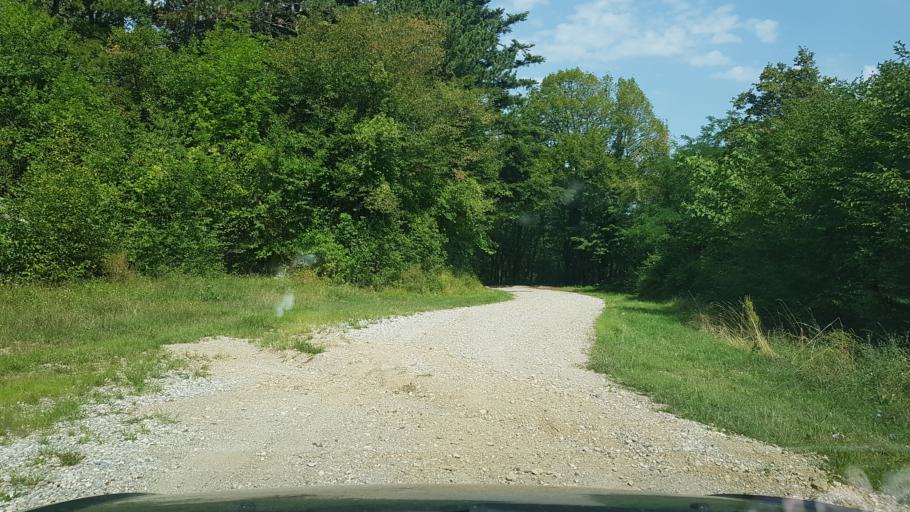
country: SI
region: Nova Gorica
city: Solkan
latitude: 46.0024
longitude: 13.6525
